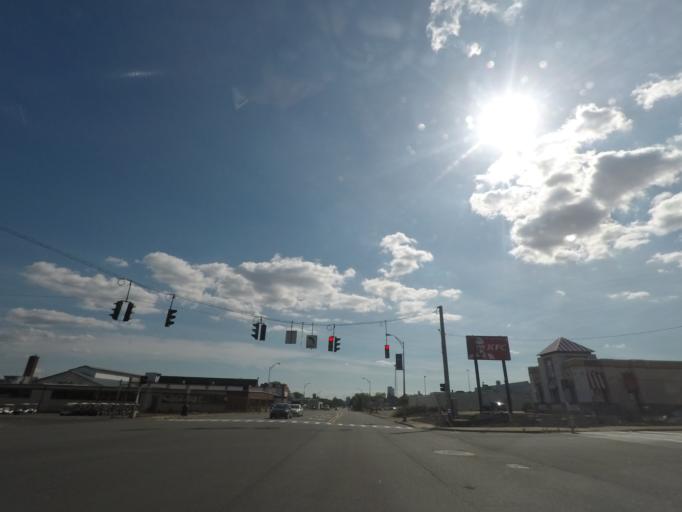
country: US
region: New York
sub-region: Albany County
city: Menands
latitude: 42.6837
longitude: -73.7310
